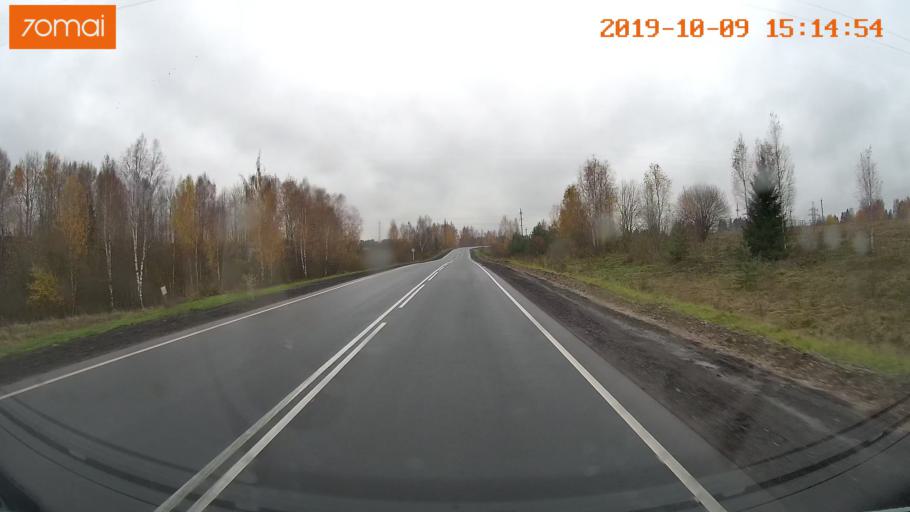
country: RU
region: Kostroma
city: Susanino
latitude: 58.1284
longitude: 41.5995
